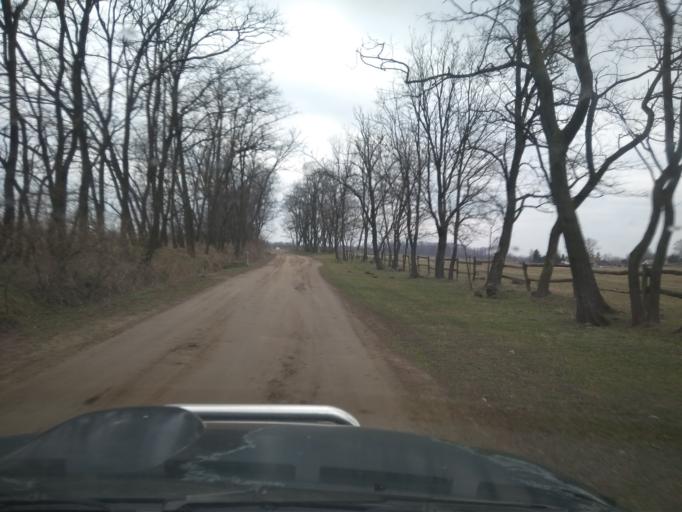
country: HU
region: Szabolcs-Szatmar-Bereg
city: Nyiregyhaza
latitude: 47.9665
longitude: 21.6636
